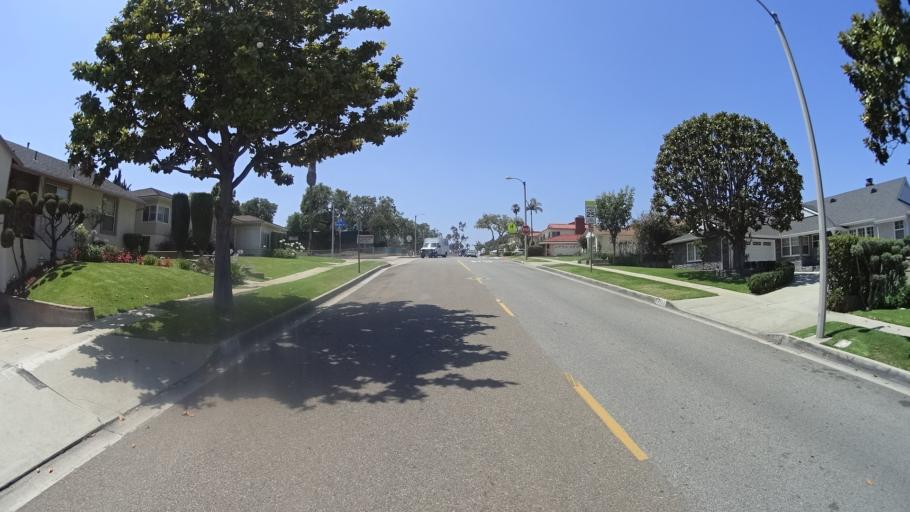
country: US
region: California
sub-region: Los Angeles County
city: View Park-Windsor Hills
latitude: 33.9955
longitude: -118.3547
